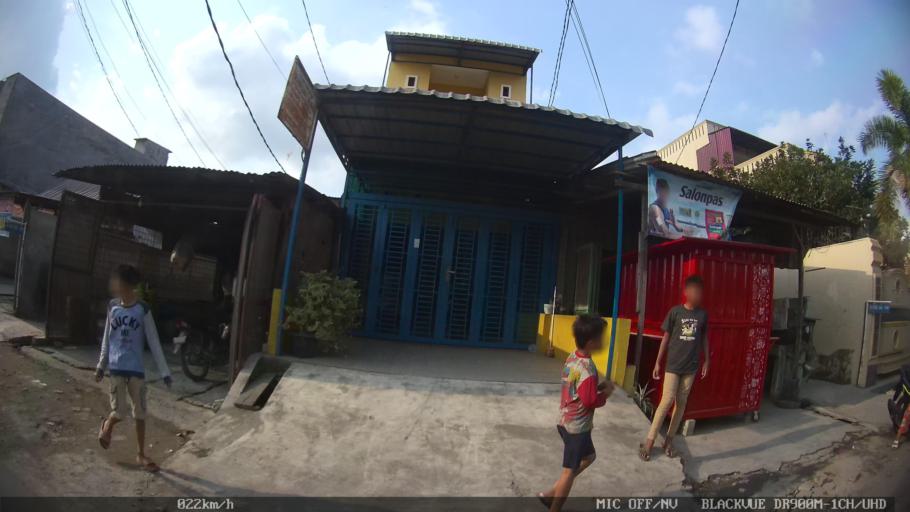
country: ID
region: North Sumatra
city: Medan
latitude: 3.5853
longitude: 98.7443
